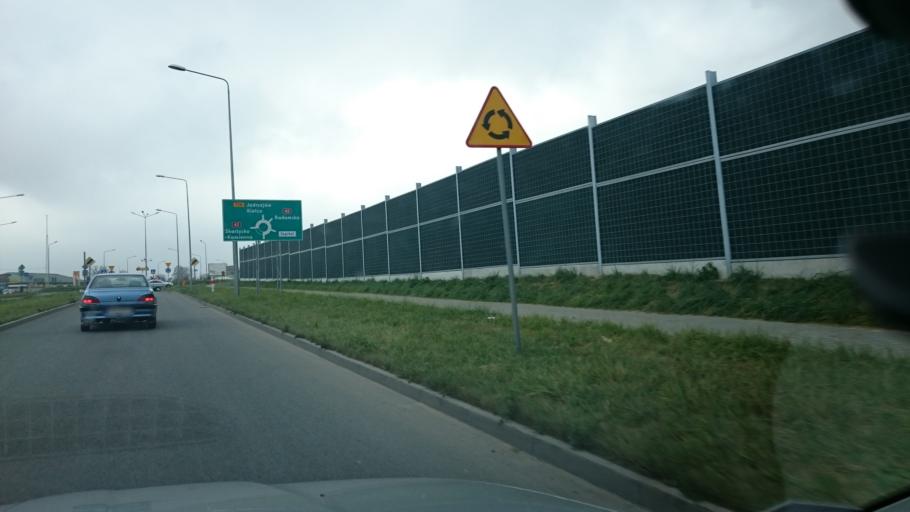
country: PL
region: Swietokrzyskie
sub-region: Powiat konecki
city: Konskie
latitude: 51.1917
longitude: 20.3984
